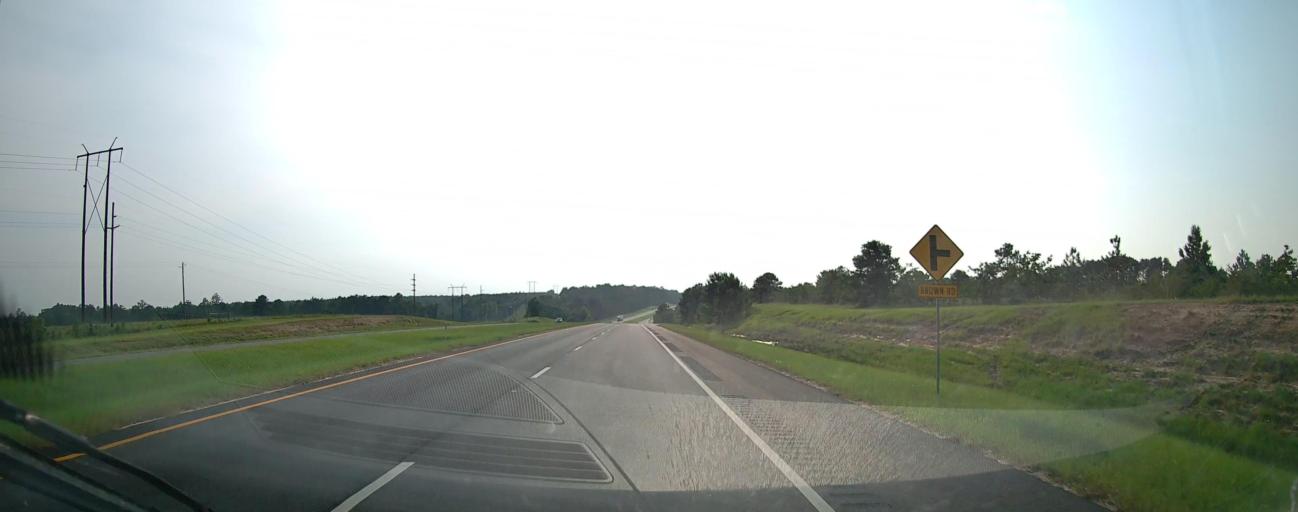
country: US
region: Georgia
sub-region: Taylor County
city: Butler
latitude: 32.5927
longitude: -84.3895
